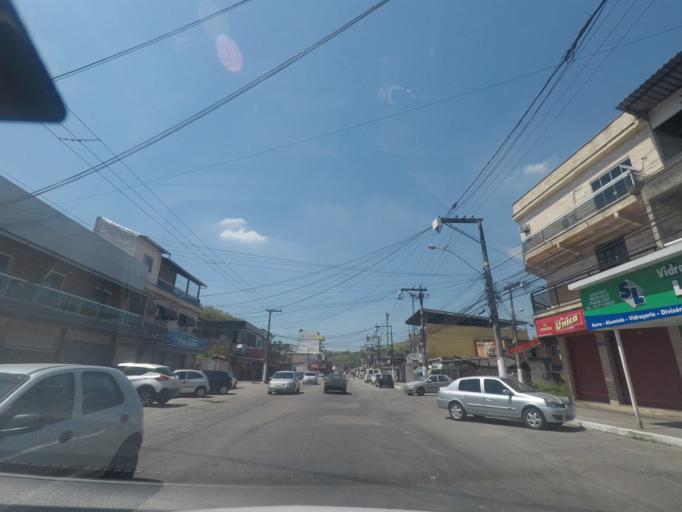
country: BR
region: Rio de Janeiro
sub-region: Petropolis
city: Petropolis
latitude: -22.5936
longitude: -43.1870
